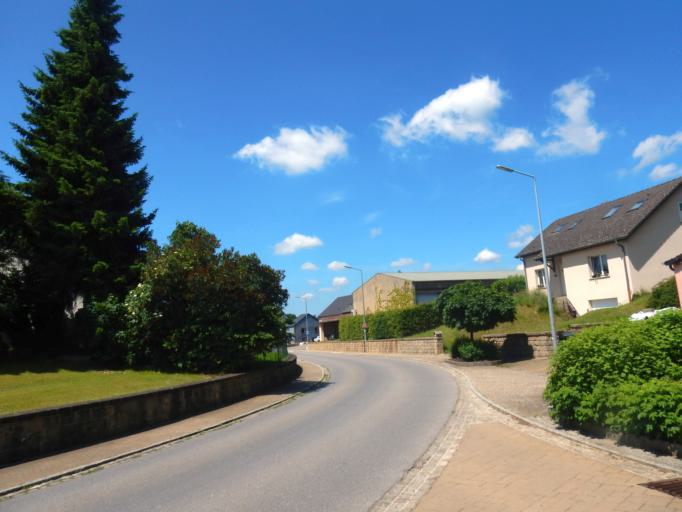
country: LU
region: Luxembourg
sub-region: Canton de Mersch
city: Tuntange
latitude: 49.7371
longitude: 6.0206
